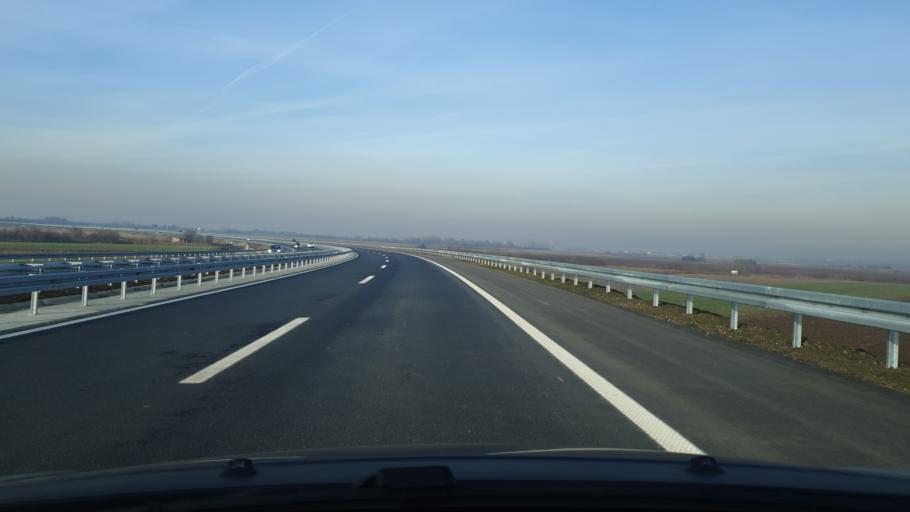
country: RS
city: Boljevci
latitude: 44.7201
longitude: 20.2581
